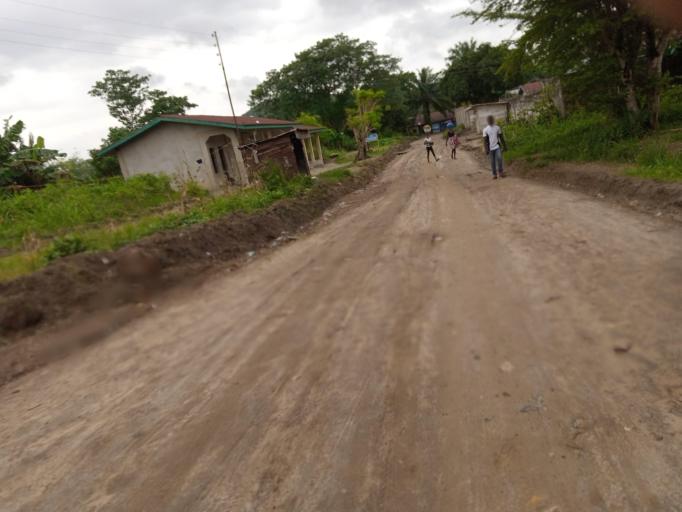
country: SL
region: Eastern Province
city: Kenema
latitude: 7.8589
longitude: -11.1980
